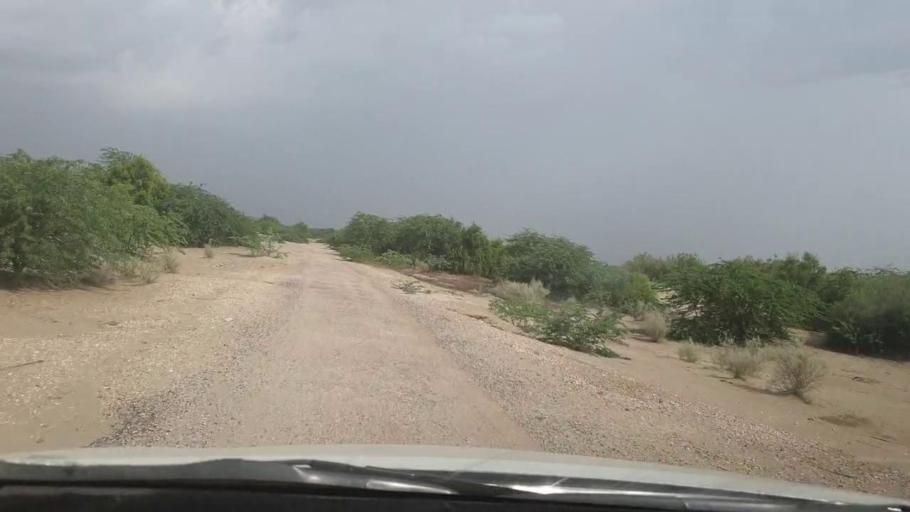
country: PK
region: Sindh
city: Kot Diji
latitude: 27.3349
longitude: 69.0468
